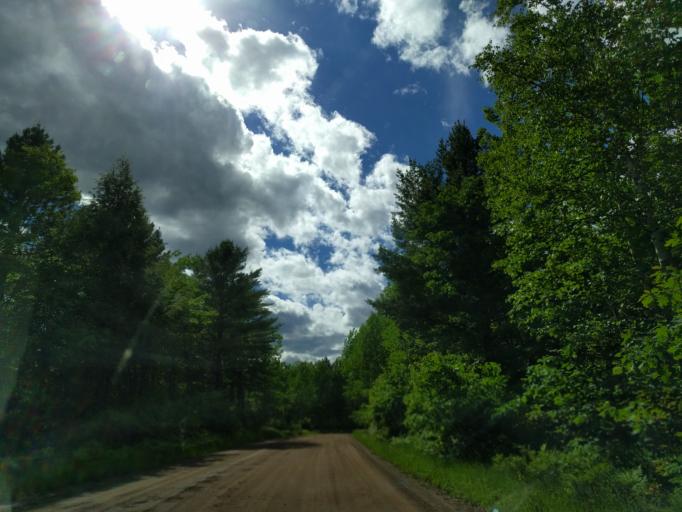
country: US
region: Michigan
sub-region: Marquette County
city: Gwinn
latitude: 46.2696
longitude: -87.3654
